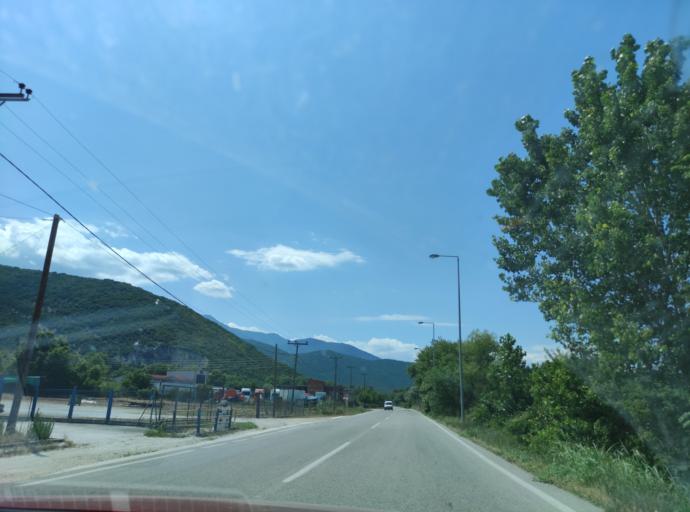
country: GR
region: East Macedonia and Thrace
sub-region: Nomos Kavalas
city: Palaiochori
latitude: 40.9516
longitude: 24.2029
